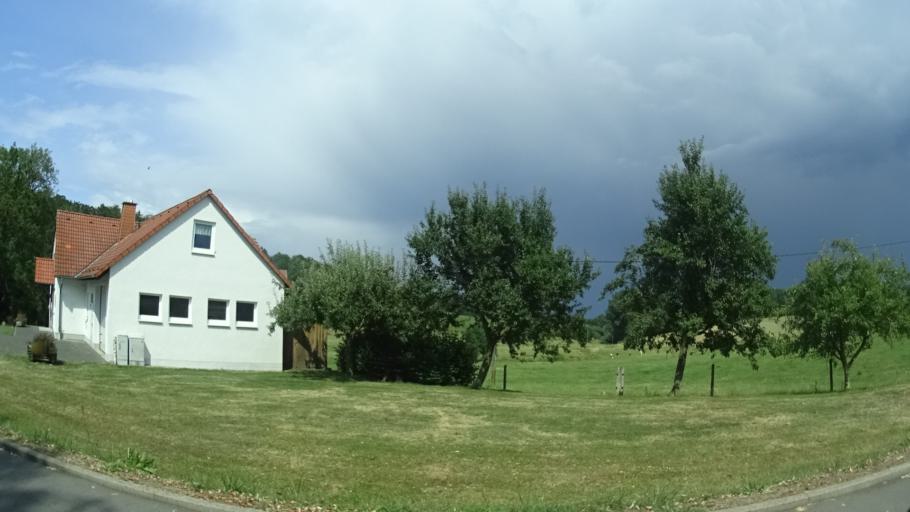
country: DE
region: Hesse
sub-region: Regierungsbezirk Giessen
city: Lauterbach
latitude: 50.5976
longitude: 9.4165
